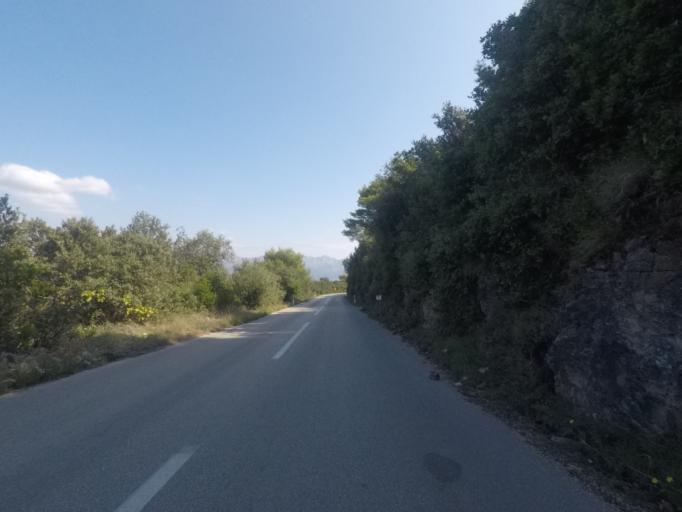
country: HR
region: Dubrovacko-Neretvanska
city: Orebic
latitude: 43.1336
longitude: 17.1438
